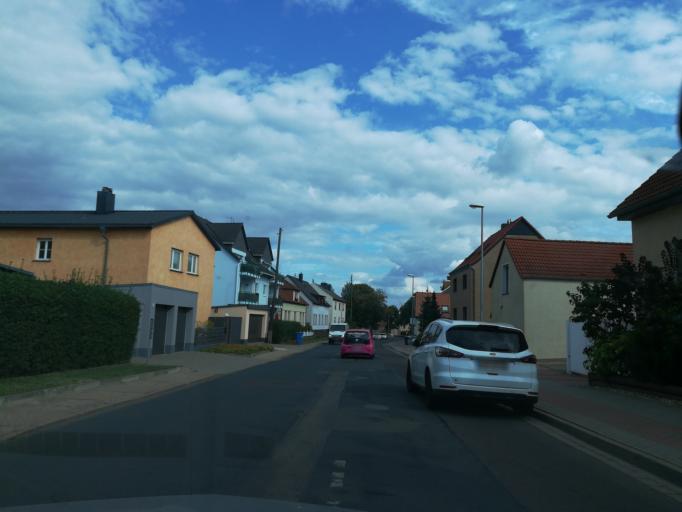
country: DE
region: Saxony-Anhalt
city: Diesdorf
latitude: 52.1308
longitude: 11.5615
